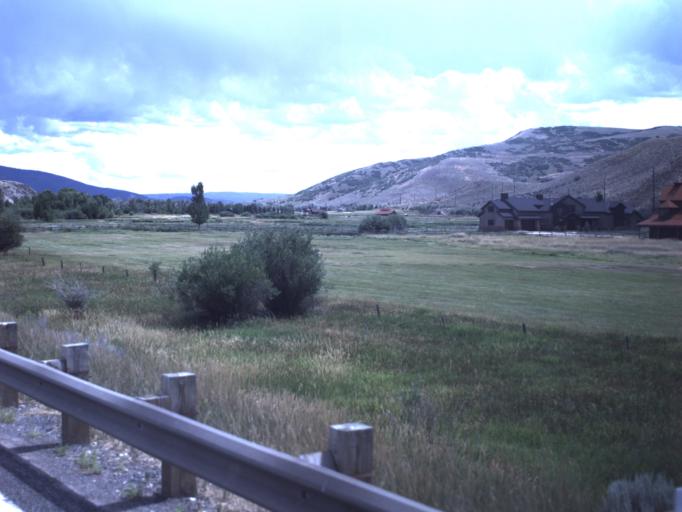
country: US
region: Utah
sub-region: Summit County
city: Oakley
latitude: 40.7521
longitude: -111.3739
